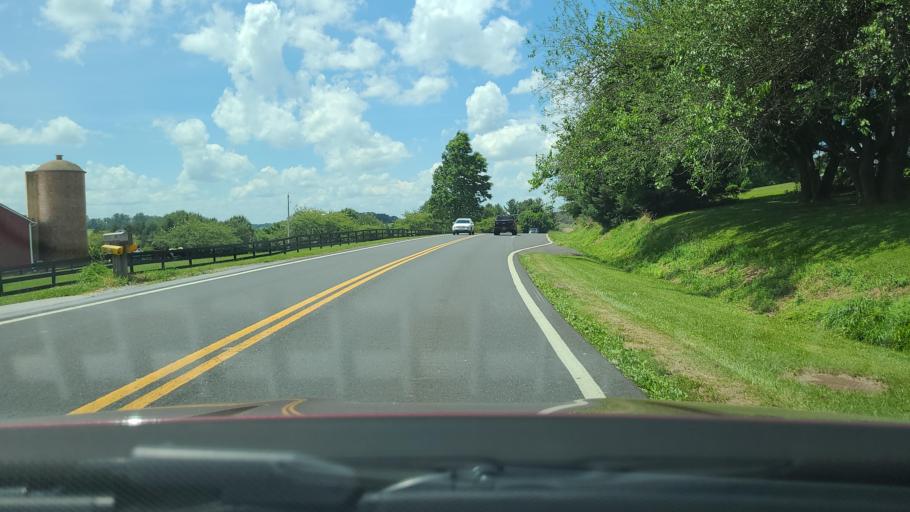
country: US
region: Maryland
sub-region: Carroll County
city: Westminster
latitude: 39.5383
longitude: -76.9999
